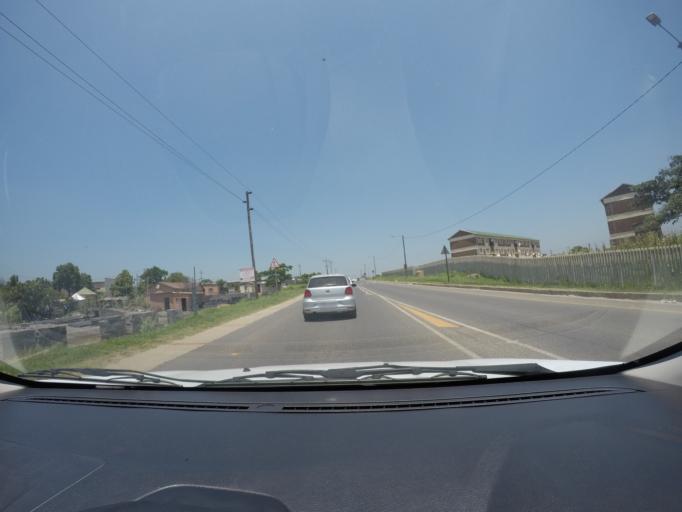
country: ZA
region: KwaZulu-Natal
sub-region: uThungulu District Municipality
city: eSikhawini
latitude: -28.8822
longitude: 31.9052
